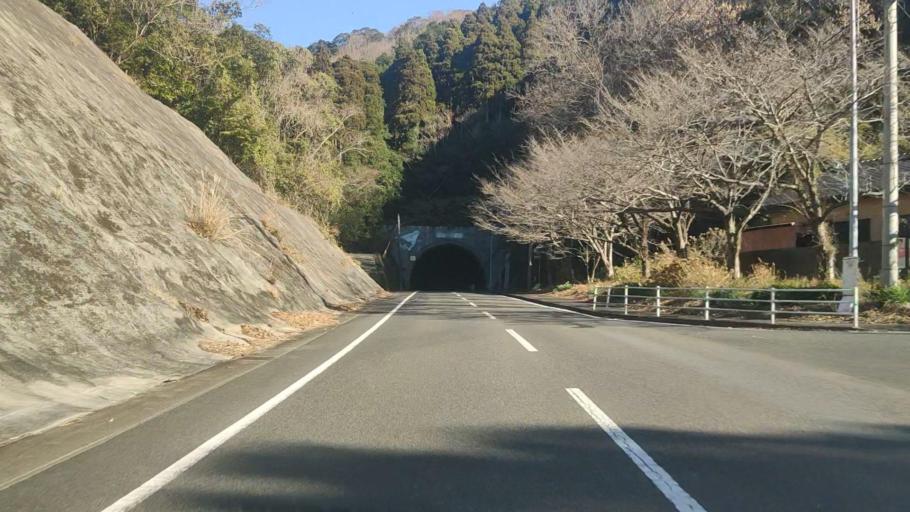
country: JP
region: Miyazaki
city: Nobeoka
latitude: 32.6906
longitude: 131.8098
